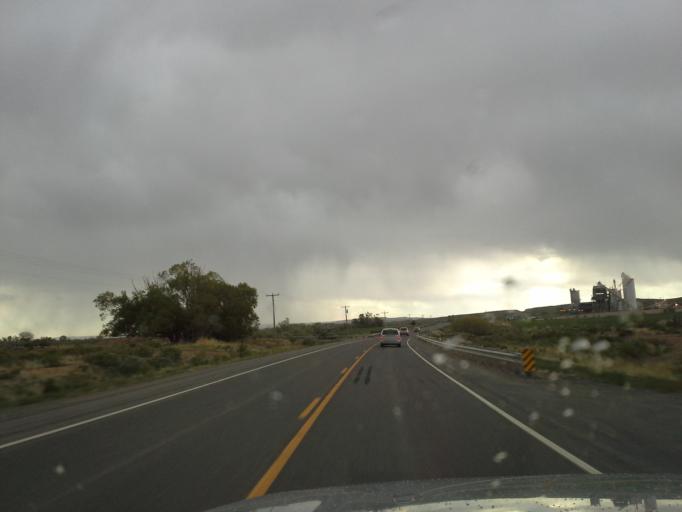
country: US
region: Wyoming
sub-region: Park County
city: Powell
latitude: 45.0060
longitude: -108.6233
